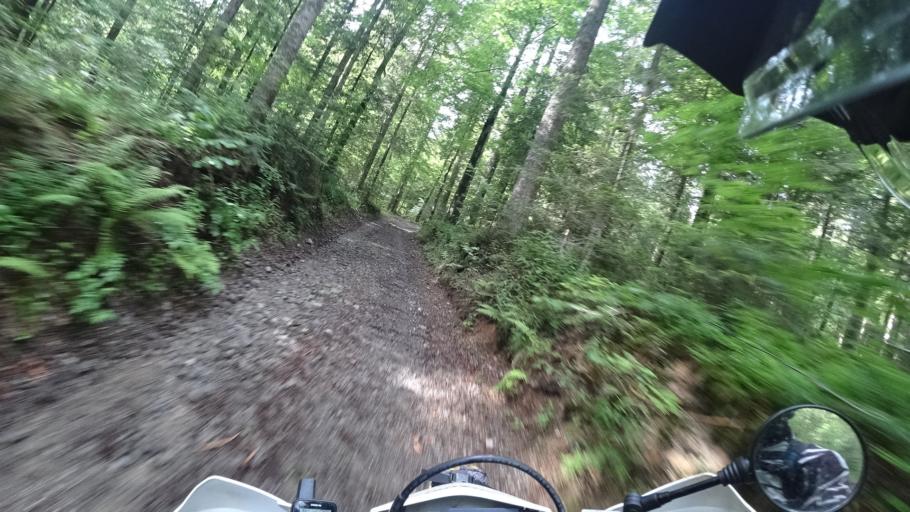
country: HR
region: Primorsko-Goranska
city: Bribir
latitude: 45.2590
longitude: 14.9153
